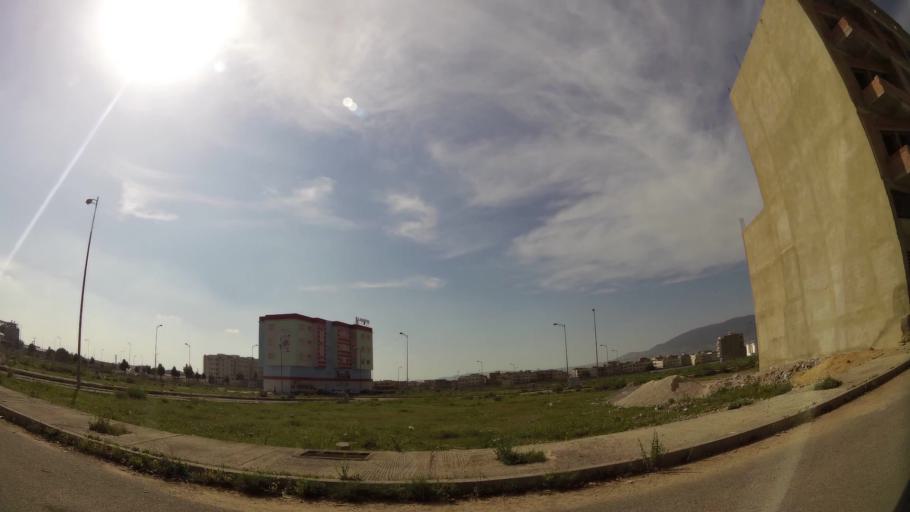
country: MA
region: Fes-Boulemane
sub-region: Fes
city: Fes
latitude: 34.0112
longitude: -5.0445
